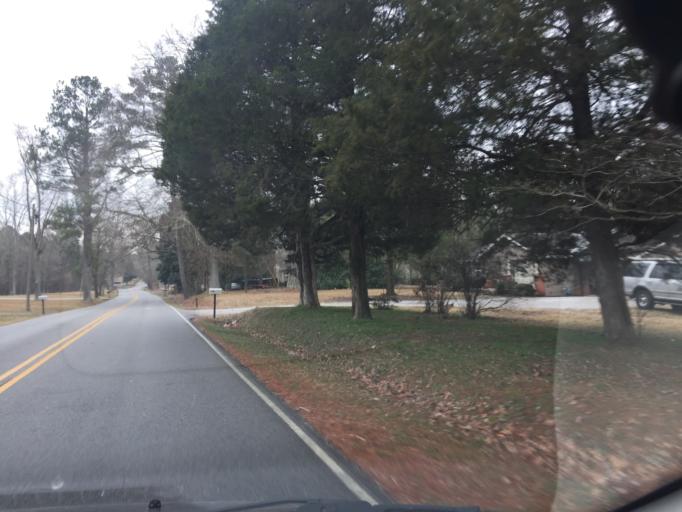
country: US
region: Georgia
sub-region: Catoosa County
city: Indian Springs
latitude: 34.9643
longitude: -85.1598
